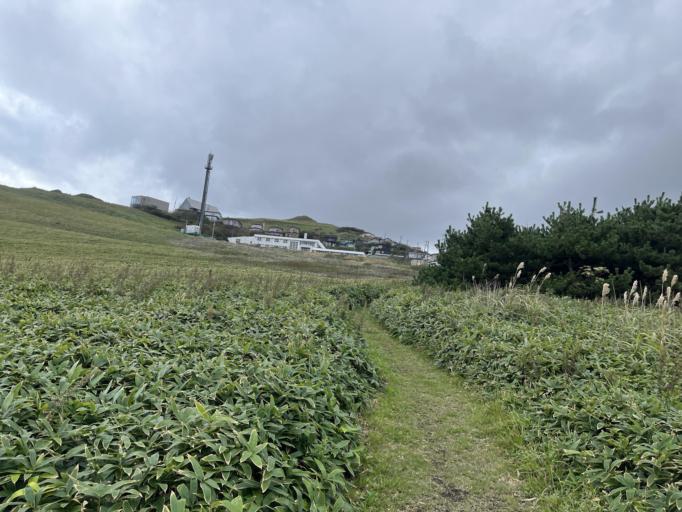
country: JP
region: Hokkaido
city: Muroran
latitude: 42.3312
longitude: 141.0190
